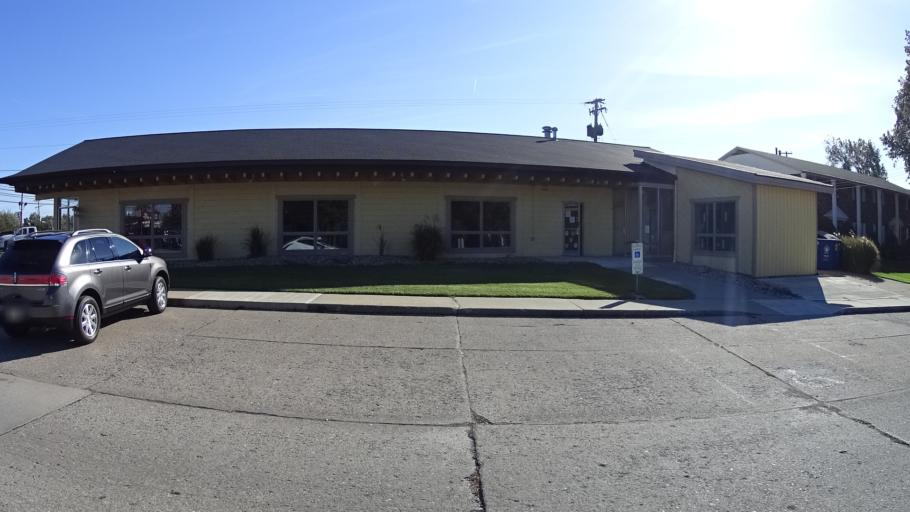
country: US
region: Ohio
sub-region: Lorain County
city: Vermilion
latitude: 41.4246
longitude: -82.3473
